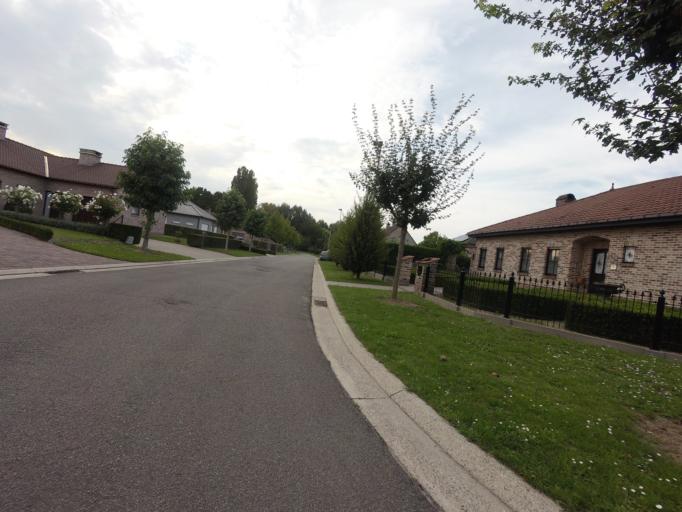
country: BE
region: Flanders
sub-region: Provincie Vlaams-Brabant
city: Boortmeerbeek
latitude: 50.9755
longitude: 4.5780
